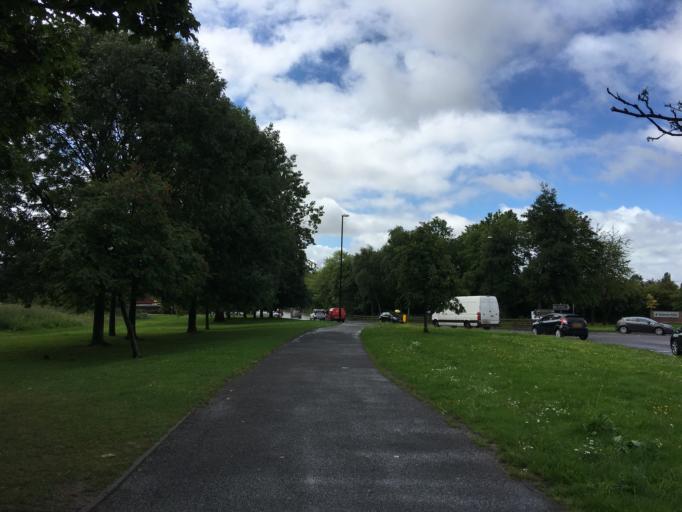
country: GB
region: England
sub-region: Coventry
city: Coventry
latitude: 52.3899
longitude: -1.5552
